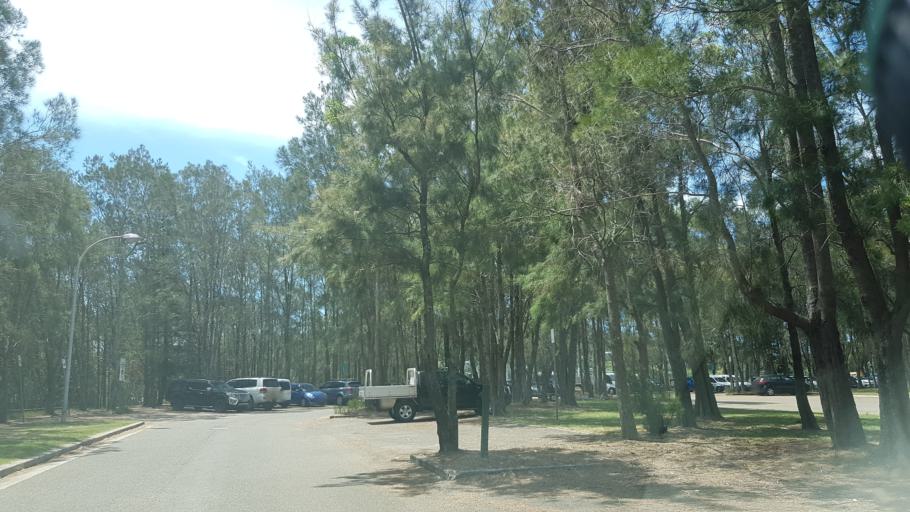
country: AU
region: New South Wales
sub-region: Pittwater
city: Bay View
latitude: -33.6620
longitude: 151.3022
